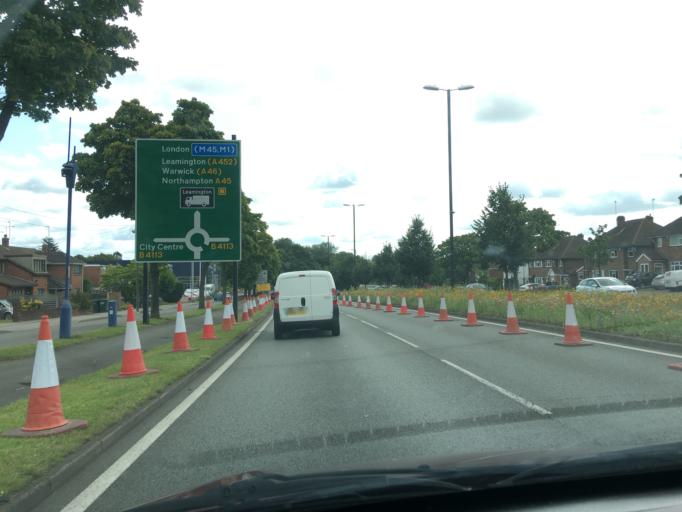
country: GB
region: England
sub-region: Coventry
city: Coventry
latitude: 52.3805
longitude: -1.5194
